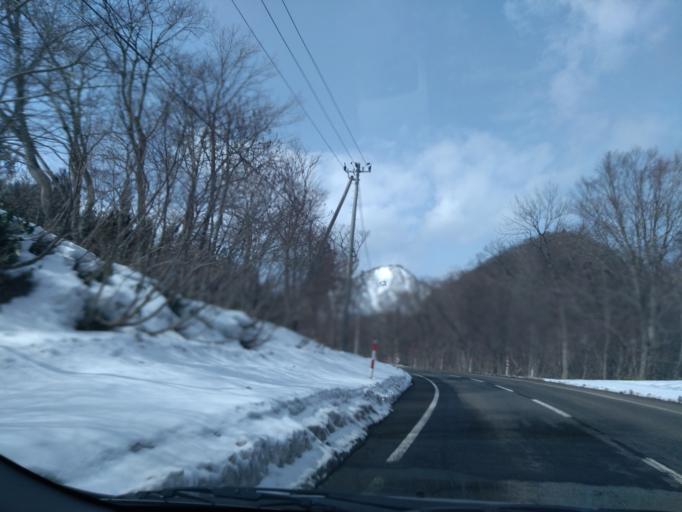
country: JP
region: Iwate
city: Kitakami
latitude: 39.2379
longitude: 140.9547
